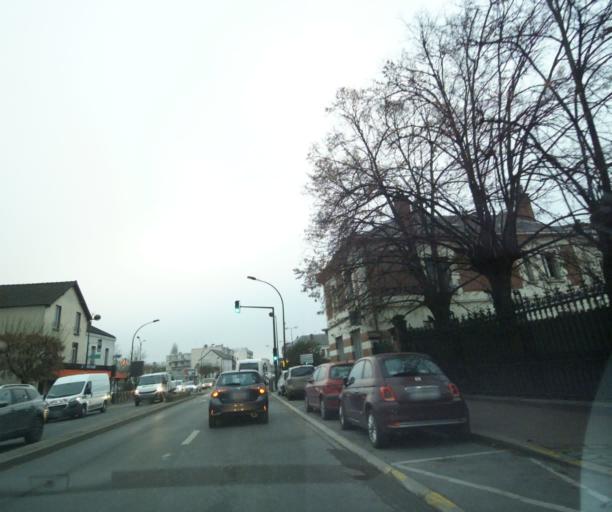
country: FR
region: Ile-de-France
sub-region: Departement de Seine-Saint-Denis
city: Livry-Gargan
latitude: 48.9195
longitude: 2.5381
